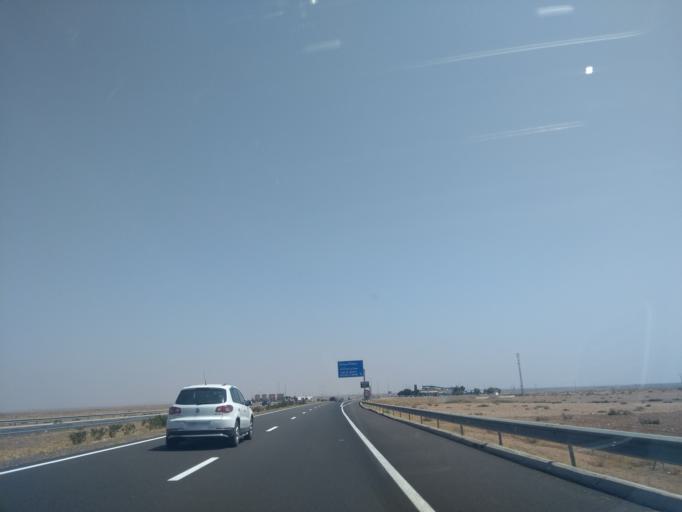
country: MA
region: Marrakech-Tensift-Al Haouz
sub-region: Kelaa-Des-Sraghna
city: Sidi Bou Othmane
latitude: 31.9141
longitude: -8.0256
